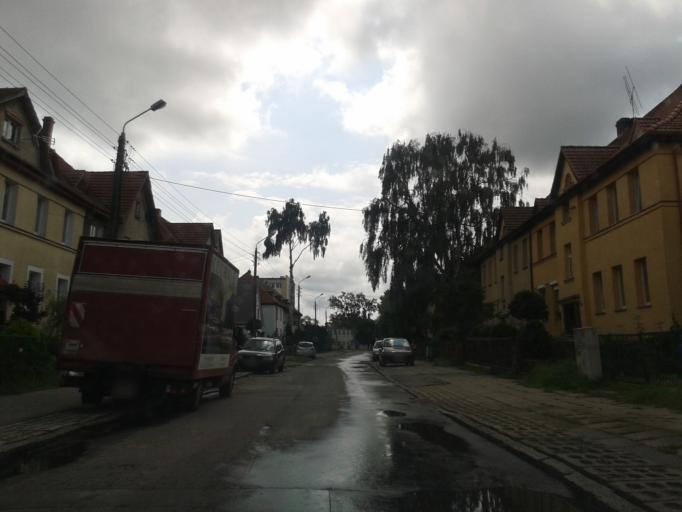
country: PL
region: West Pomeranian Voivodeship
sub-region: Swinoujscie
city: Swinoujscie
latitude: 53.9056
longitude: 14.2323
